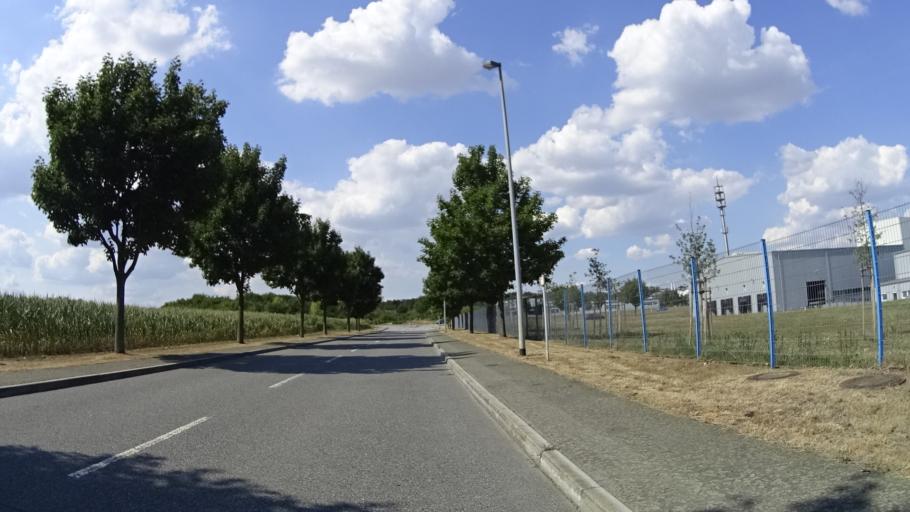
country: DE
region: Saxony
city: Zittau
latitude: 50.9059
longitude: 14.8394
